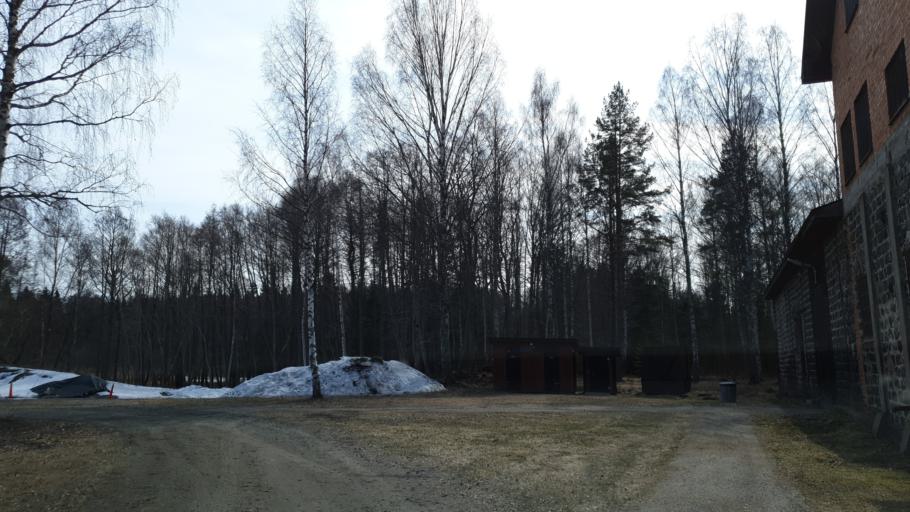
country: SE
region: Gaevleborg
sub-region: Gavle Kommun
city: Norrsundet
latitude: 61.0468
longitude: 17.1501
